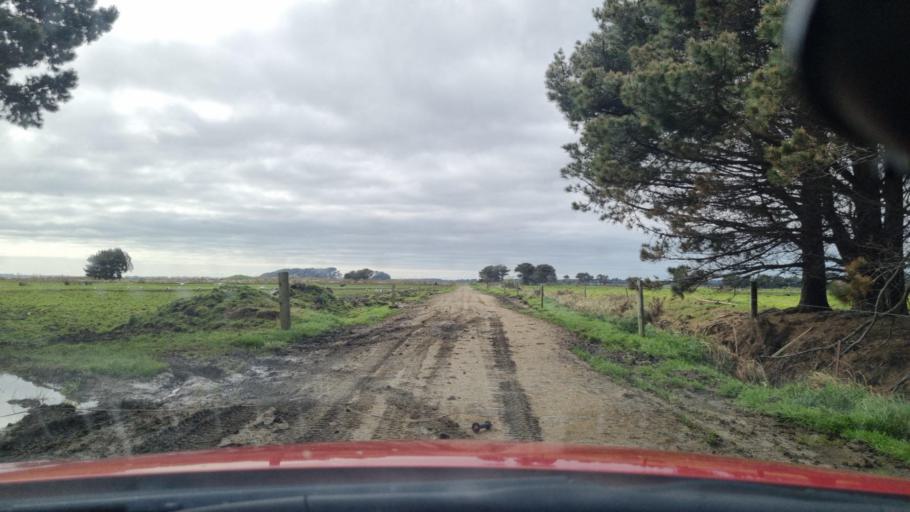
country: NZ
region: Southland
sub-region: Invercargill City
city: Bluff
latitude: -46.5155
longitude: 168.3032
